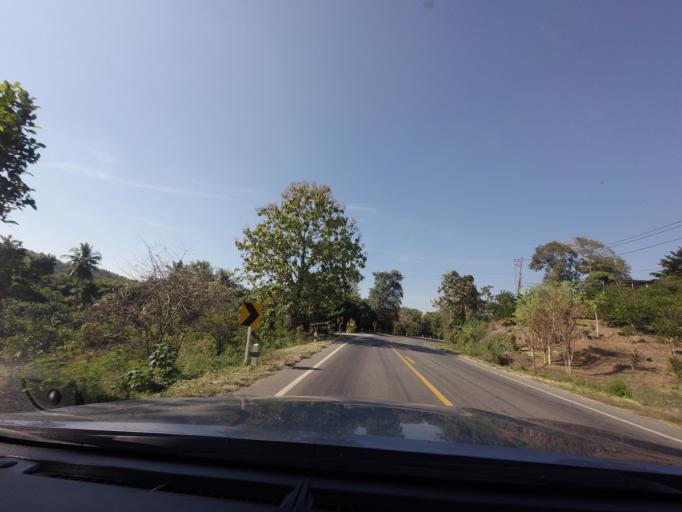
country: TH
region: Sukhothai
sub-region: Amphoe Si Satchanalai
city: Si Satchanalai
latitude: 17.6243
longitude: 99.7022
